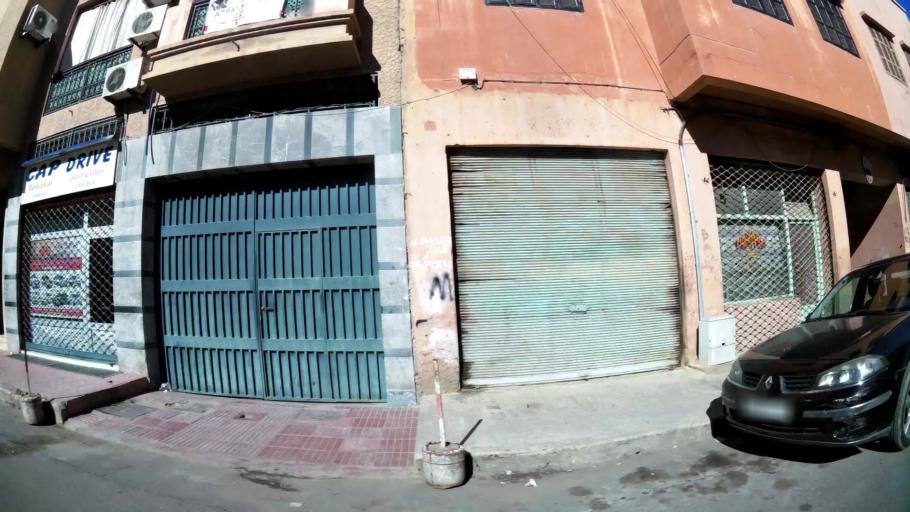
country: MA
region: Marrakech-Tensift-Al Haouz
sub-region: Marrakech
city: Marrakesh
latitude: 31.6388
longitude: -8.0174
